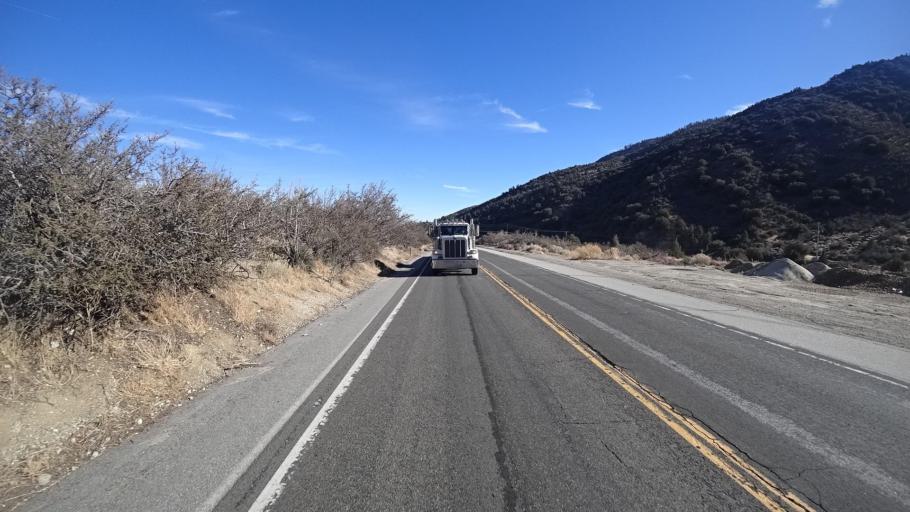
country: US
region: California
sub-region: Kern County
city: Frazier Park
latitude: 34.8204
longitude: -118.9641
